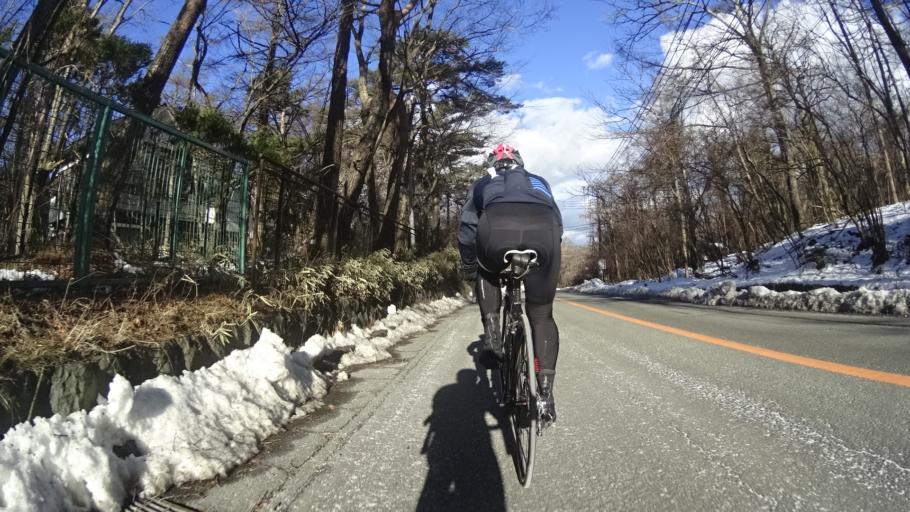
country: JP
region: Shizuoka
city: Gotemba
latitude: 35.4020
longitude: 138.8738
